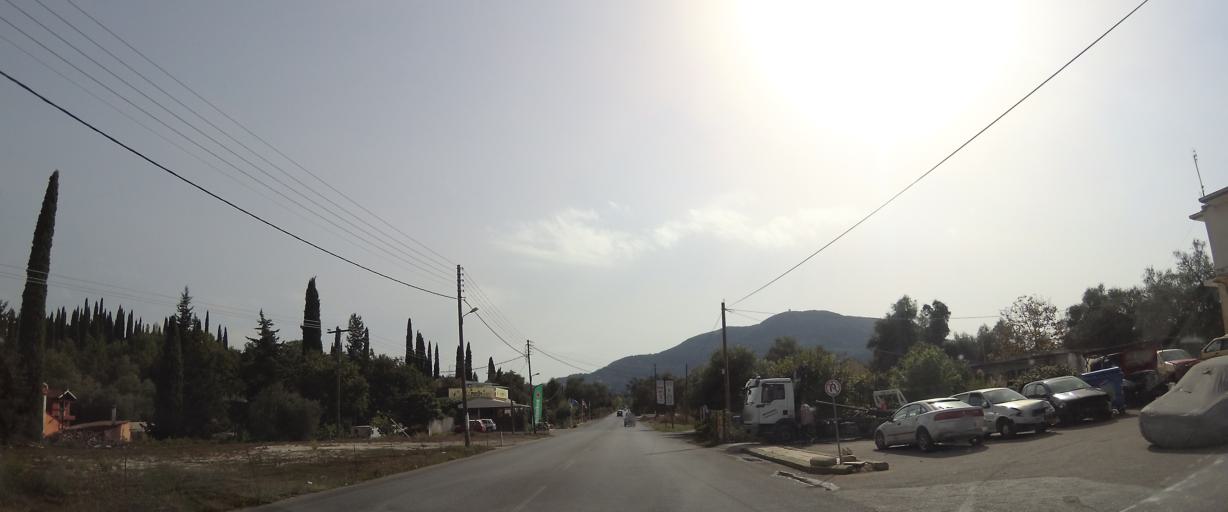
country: GR
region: Ionian Islands
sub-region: Nomos Kerkyras
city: Viros
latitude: 39.5767
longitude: 19.8930
